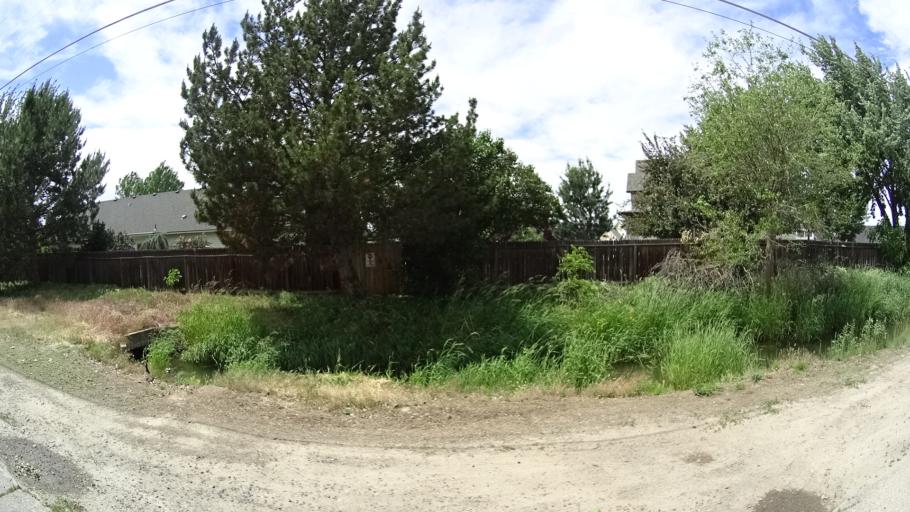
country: US
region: Idaho
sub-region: Ada County
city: Meridian
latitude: 43.6248
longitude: -116.3203
